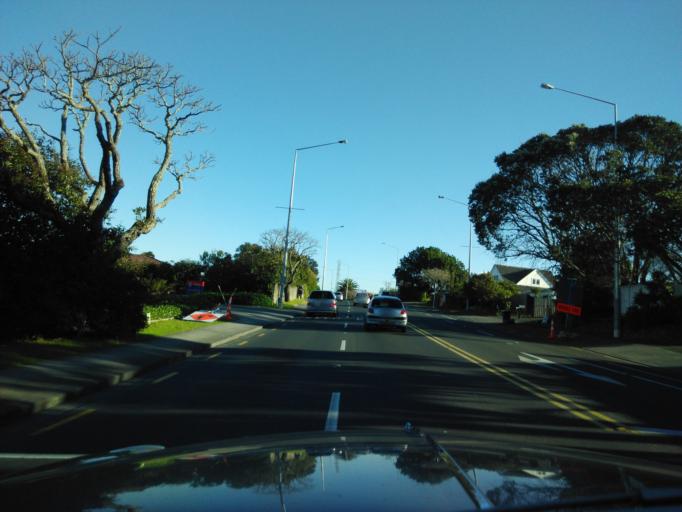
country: NZ
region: Auckland
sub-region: Auckland
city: Rosebank
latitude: -36.8601
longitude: 174.6510
